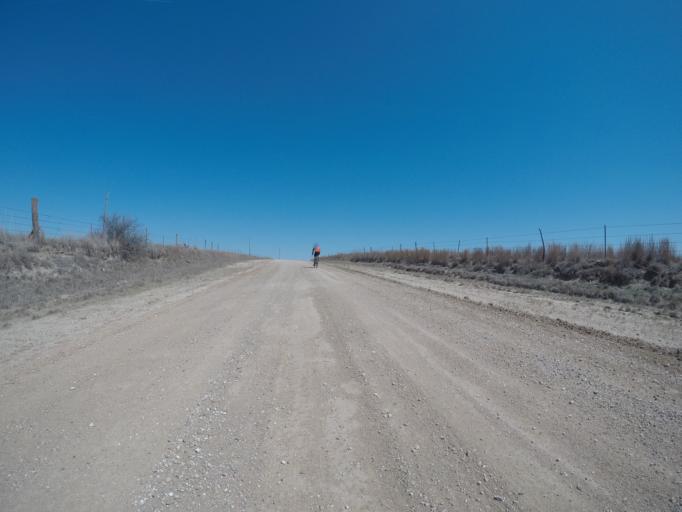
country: US
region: Kansas
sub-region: Pratt County
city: Pratt
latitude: 37.4065
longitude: -98.8405
